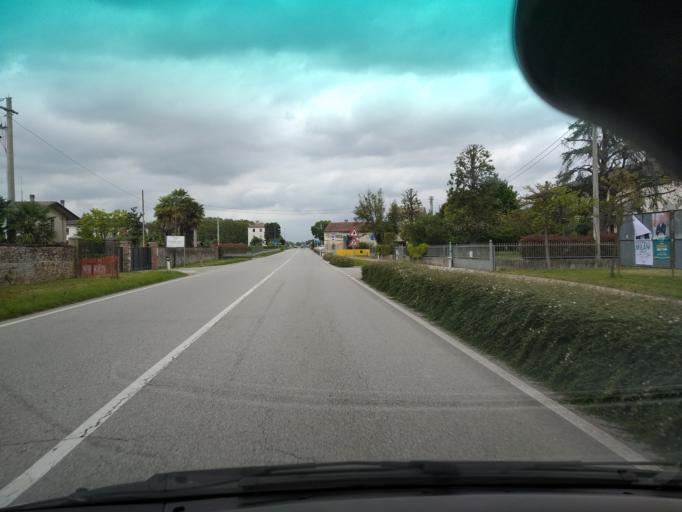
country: IT
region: Veneto
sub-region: Provincia di Padova
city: Tremignon
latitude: 45.5226
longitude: 11.7998
